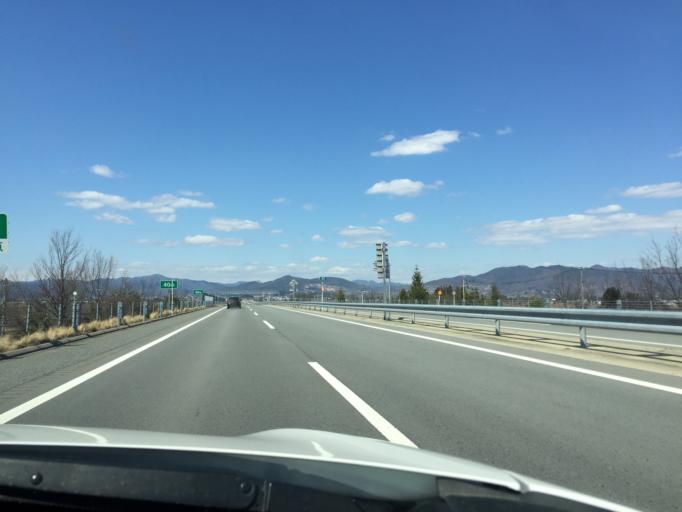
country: JP
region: Yamagata
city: Takahata
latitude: 37.9964
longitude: 140.1563
